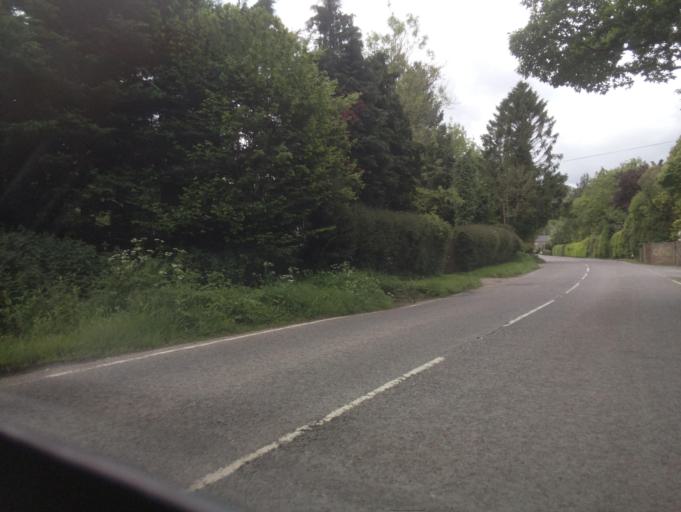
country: GB
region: England
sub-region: Dorset
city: Sherborne
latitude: 50.8531
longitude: -2.4813
